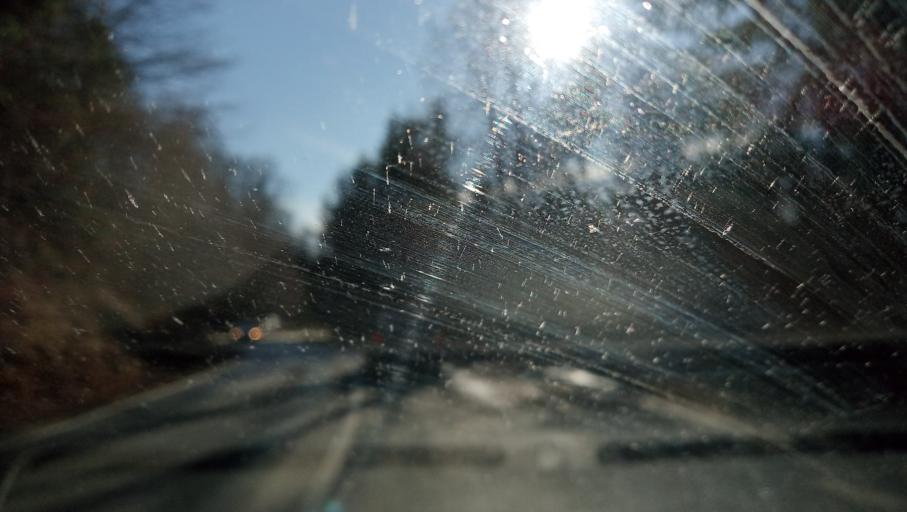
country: RO
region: Brasov
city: Crivina
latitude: 45.4703
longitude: 25.9349
